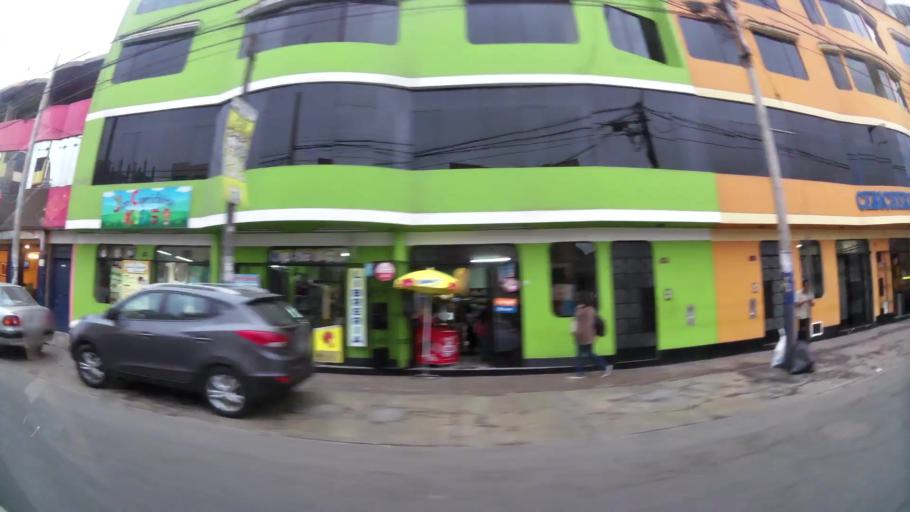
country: PE
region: Lima
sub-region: Lima
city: San Luis
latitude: -12.0753
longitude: -76.9781
